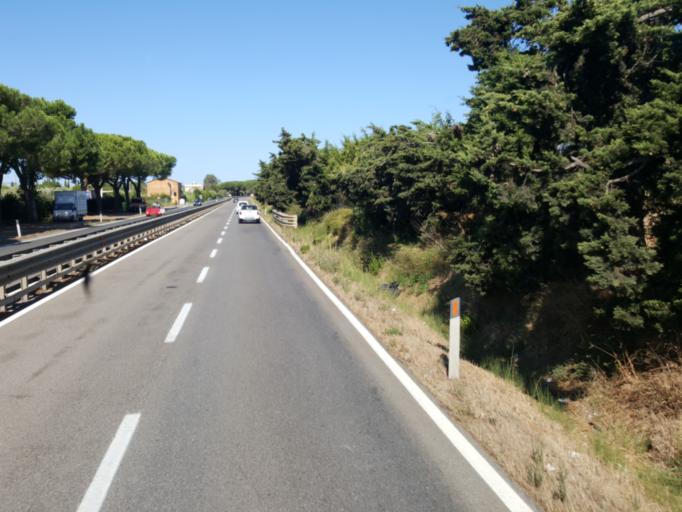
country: IT
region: Tuscany
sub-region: Provincia di Grosseto
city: Orbetello Scalo
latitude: 42.4399
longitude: 11.2689
